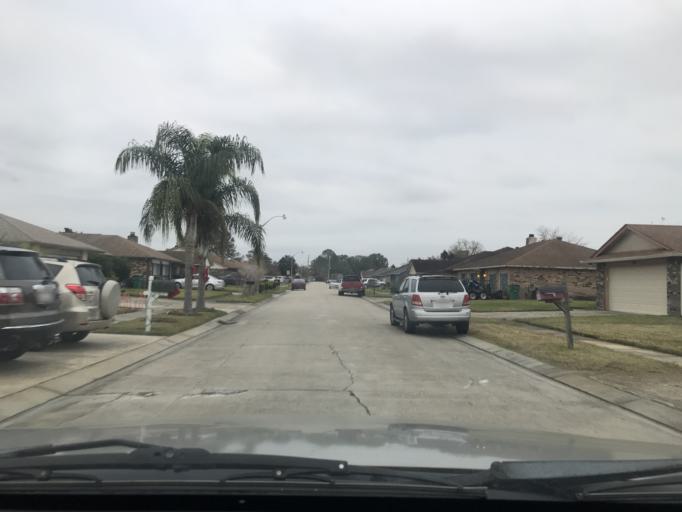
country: US
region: Louisiana
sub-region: Jefferson Parish
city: Woodmere
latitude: 29.8614
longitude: -90.0843
